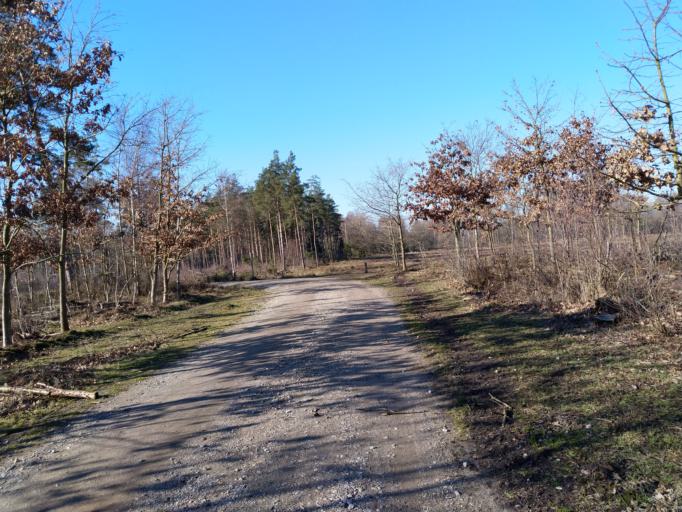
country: DK
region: Zealand
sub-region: Guldborgsund Kommune
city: Nykobing Falster
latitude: 54.6388
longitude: 11.9575
